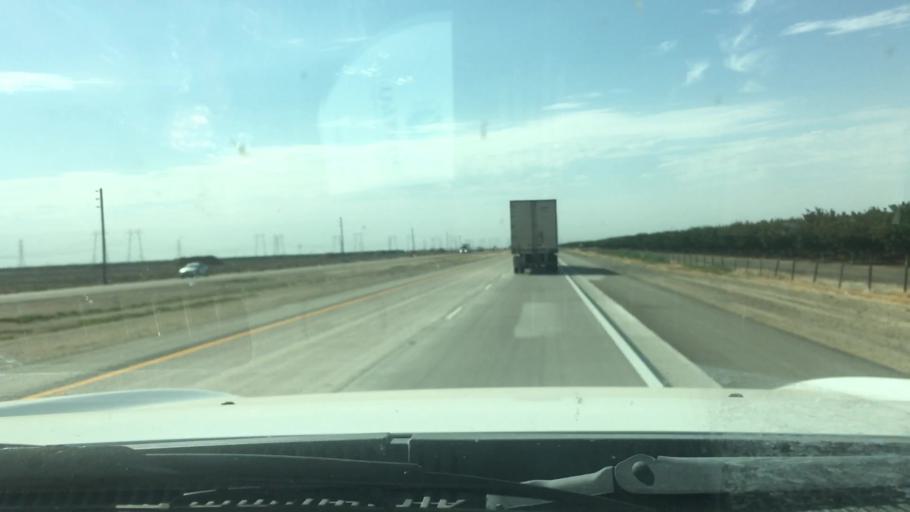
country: US
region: California
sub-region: Kern County
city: Buttonwillow
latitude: 35.5247
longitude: -119.5621
